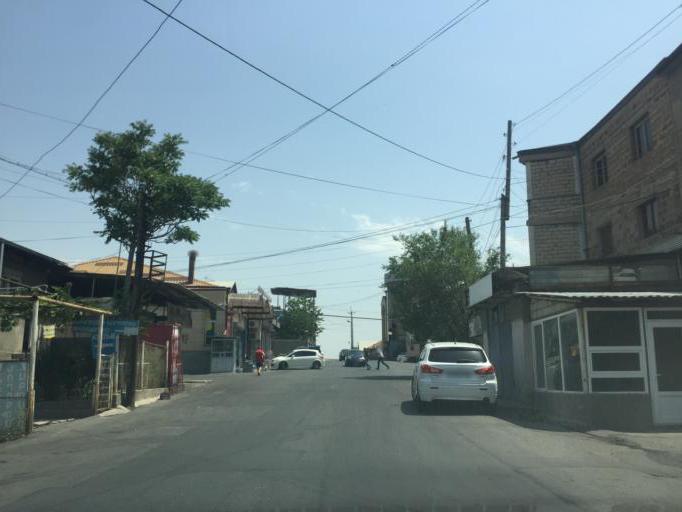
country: AM
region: Yerevan
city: Yerevan
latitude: 40.1763
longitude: 44.4908
